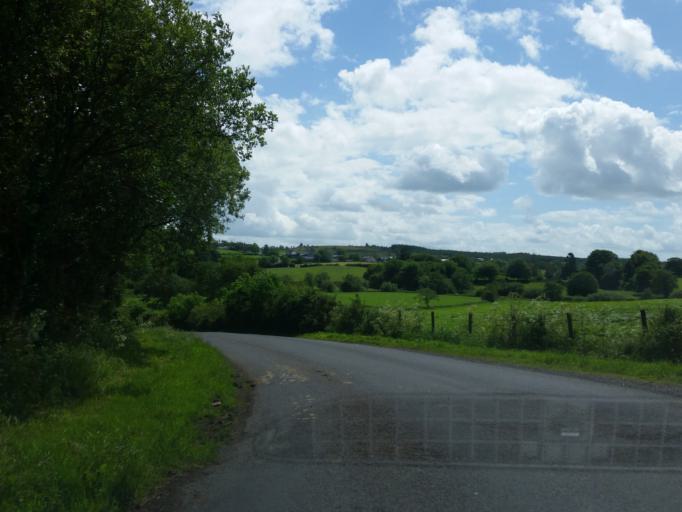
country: GB
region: Northern Ireland
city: Fivemiletown
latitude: 54.3667
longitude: -7.3114
